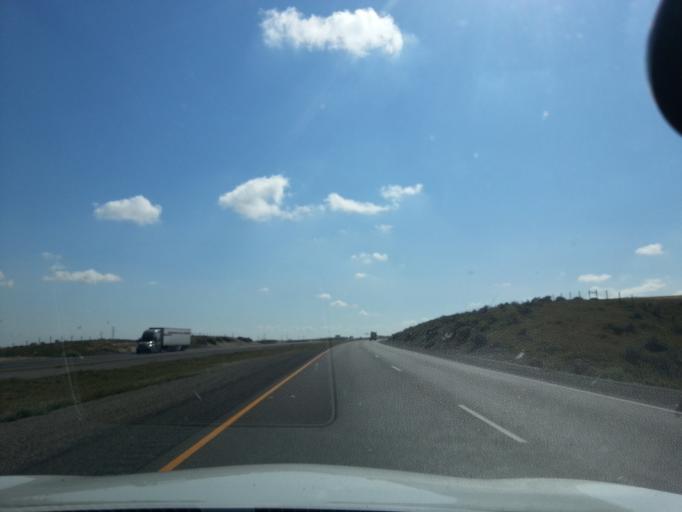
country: US
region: California
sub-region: Fresno County
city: Mendota
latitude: 36.5217
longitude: -120.4761
